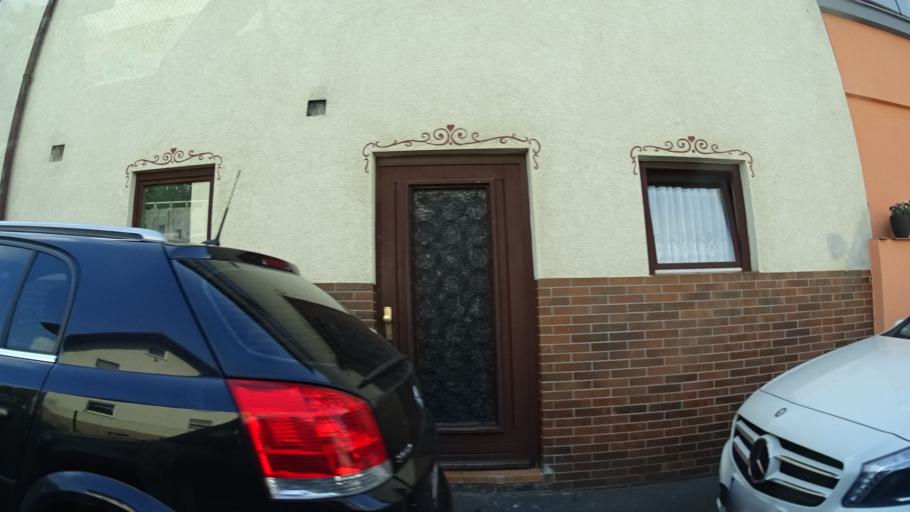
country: DE
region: Bavaria
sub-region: Regierungsbezirk Unterfranken
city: Heimbuchenthal
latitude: 49.8635
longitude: 9.3111
